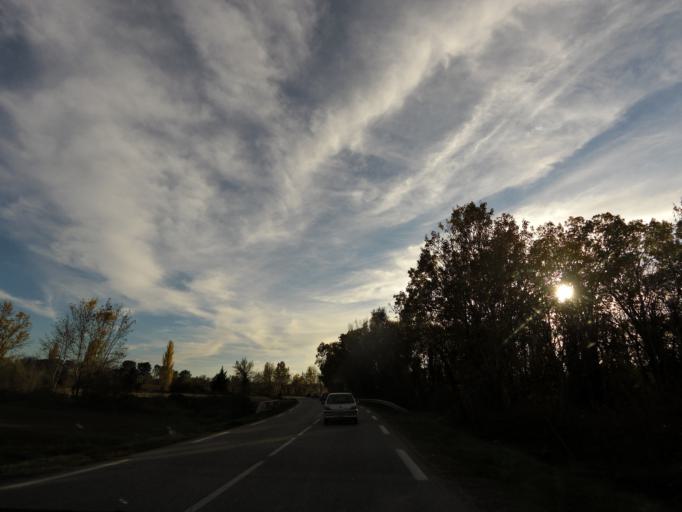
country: FR
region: Languedoc-Roussillon
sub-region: Departement du Gard
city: Ledignan
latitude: 43.9723
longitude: 4.1005
